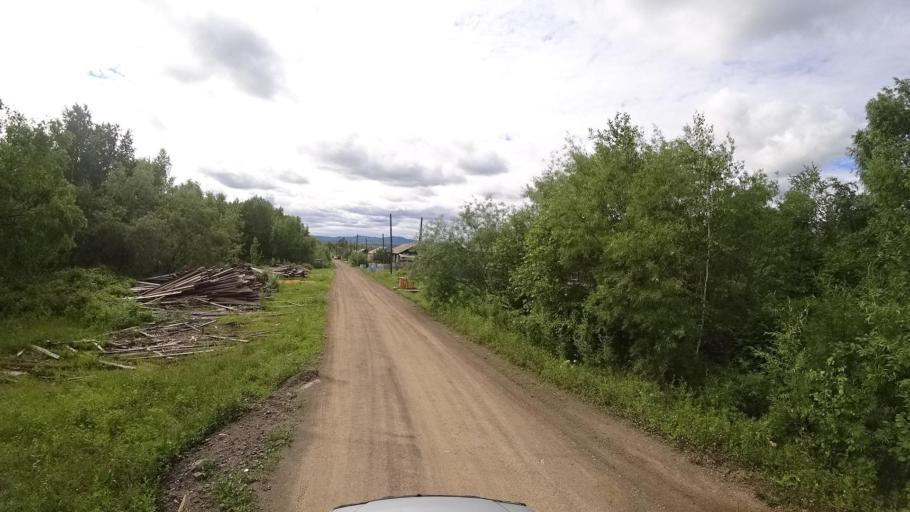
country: RU
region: Khabarovsk Krai
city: Litovko
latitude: 49.3711
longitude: 135.1803
